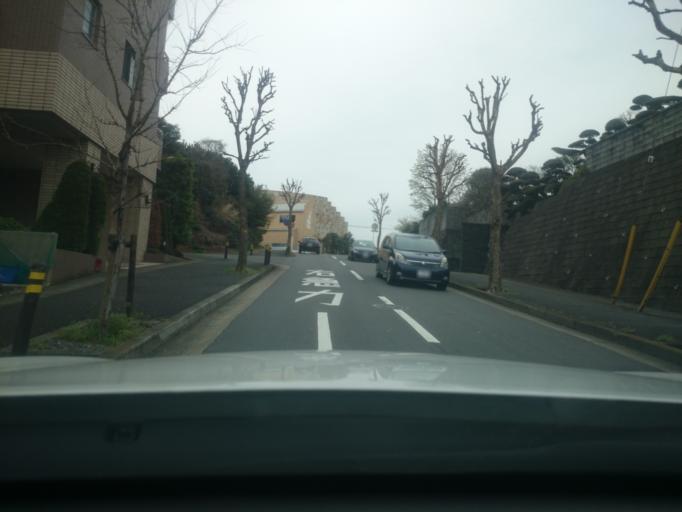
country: JP
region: Tokyo
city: Chofugaoka
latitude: 35.5703
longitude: 139.5748
